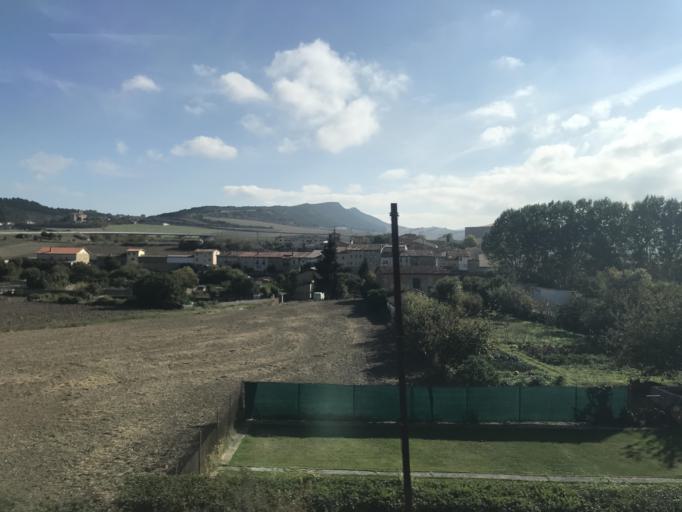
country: ES
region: Basque Country
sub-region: Provincia de Alava
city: Arminon
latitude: 42.7232
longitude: -2.8758
